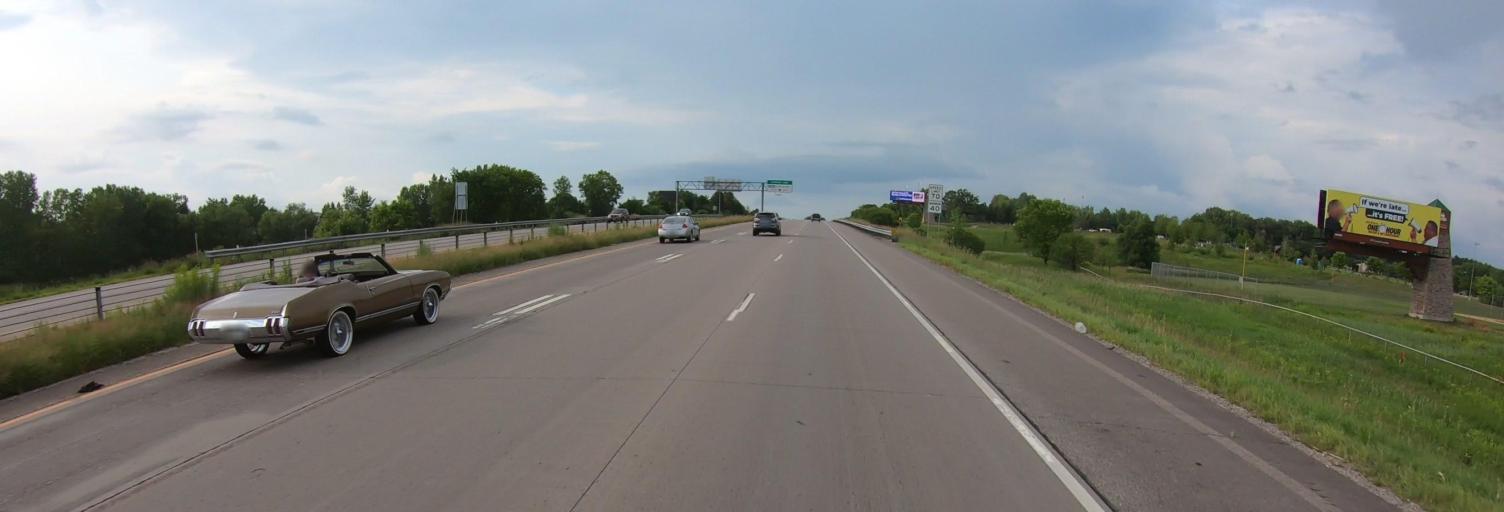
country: US
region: Minnesota
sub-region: Ramsey County
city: North Oaks
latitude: 45.0909
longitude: -93.0522
